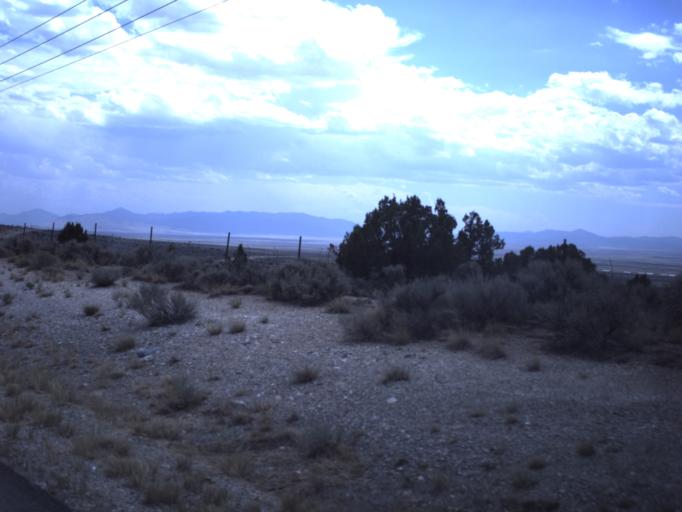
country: US
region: Utah
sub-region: Tooele County
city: Tooele
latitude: 40.3309
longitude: -112.2944
